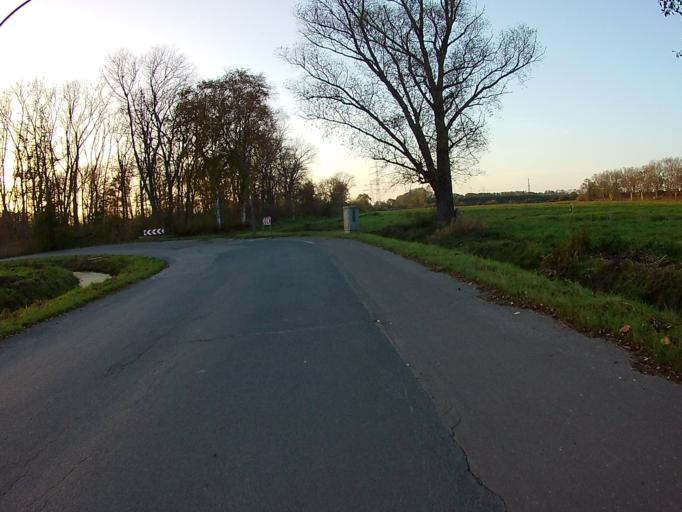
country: DE
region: Hamburg
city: Harburg
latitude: 53.4826
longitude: 9.9280
